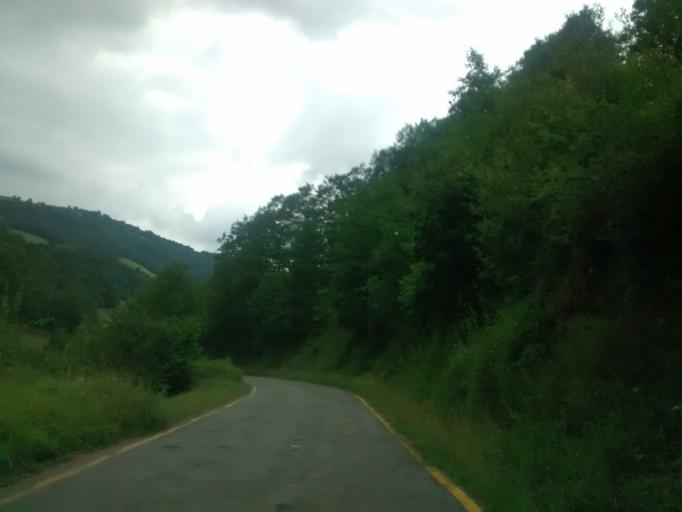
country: ES
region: Cantabria
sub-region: Provincia de Cantabria
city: Vega de Pas
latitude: 43.1430
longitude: -3.7681
